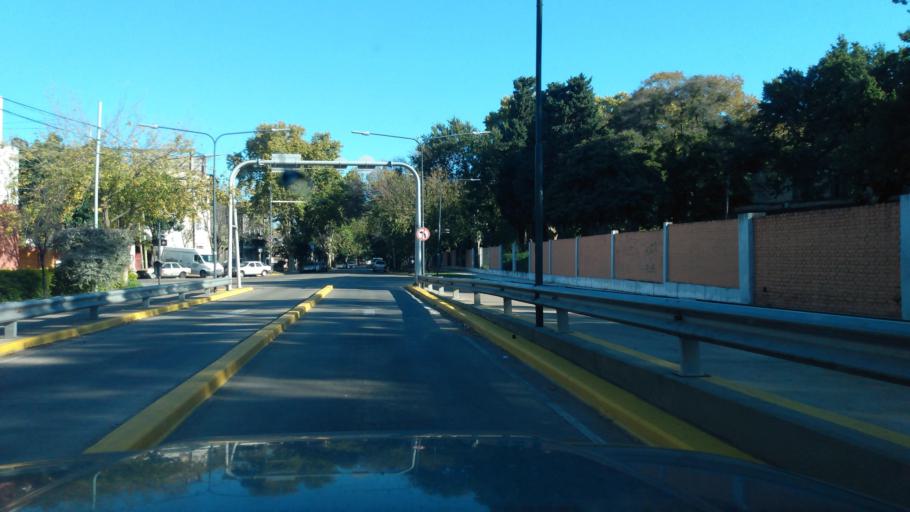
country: AR
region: Buenos Aires F.D.
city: Villa Santa Rita
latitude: -34.5931
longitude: -58.4700
